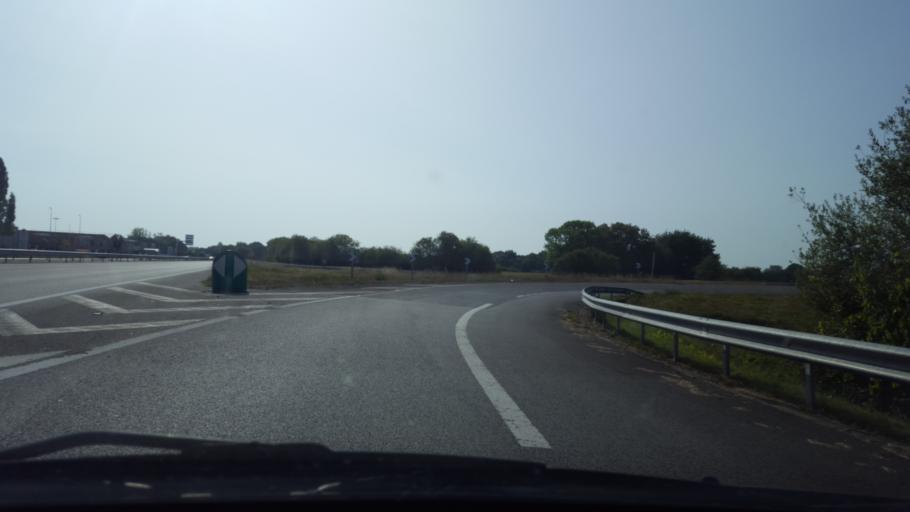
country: FR
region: Pays de la Loire
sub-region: Departement de la Loire-Atlantique
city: Saint-Philbert-de-Grand-Lieu
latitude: 47.0484
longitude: -1.6381
